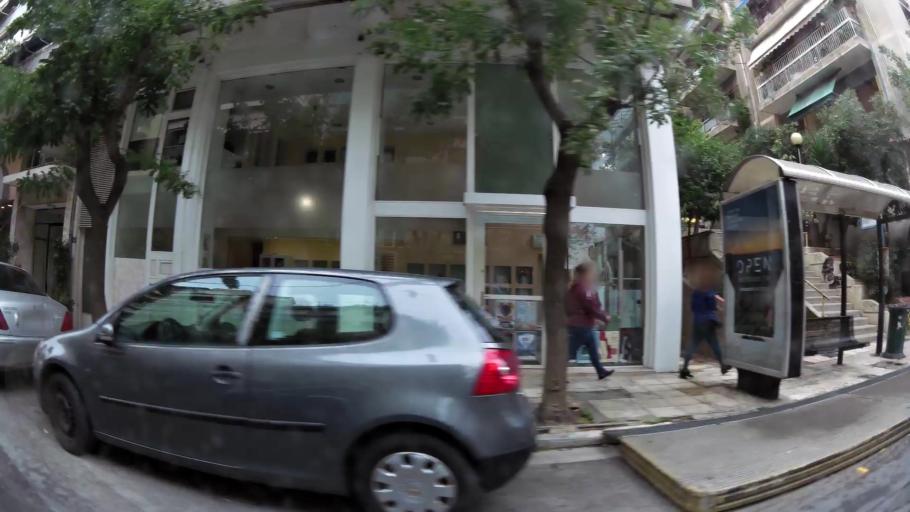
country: GR
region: Attica
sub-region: Nomarchia Athinas
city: Vyronas
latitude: 37.9697
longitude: 23.7522
